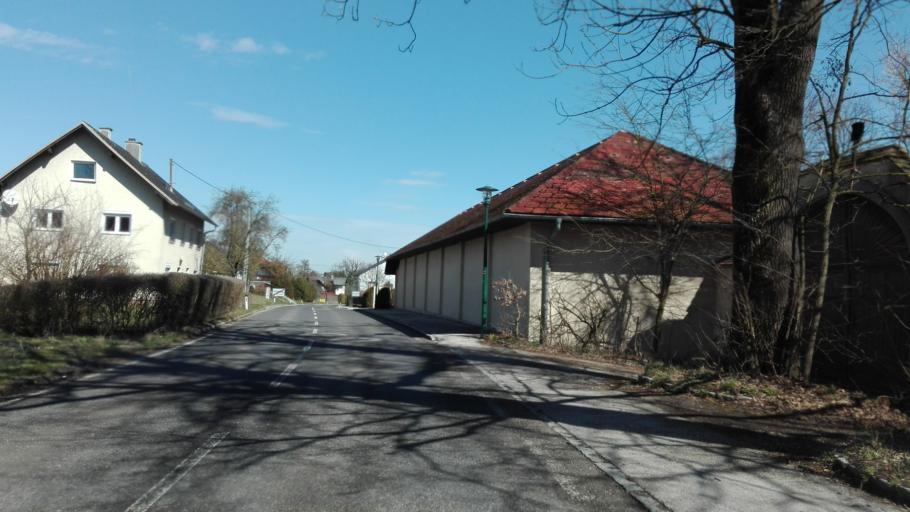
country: AT
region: Upper Austria
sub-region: Politischer Bezirk Grieskirchen
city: Bad Schallerbach
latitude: 48.1961
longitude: 13.9523
